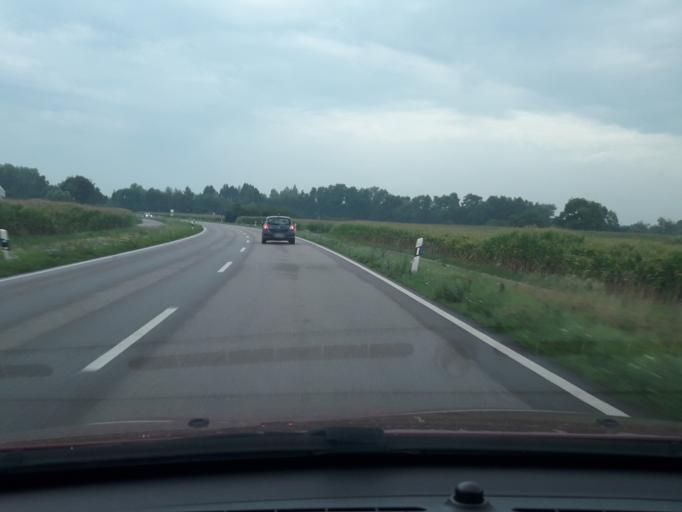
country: DE
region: Baden-Wuerttemberg
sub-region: Freiburg Region
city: Rheinau
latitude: 48.6702
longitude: 7.9225
